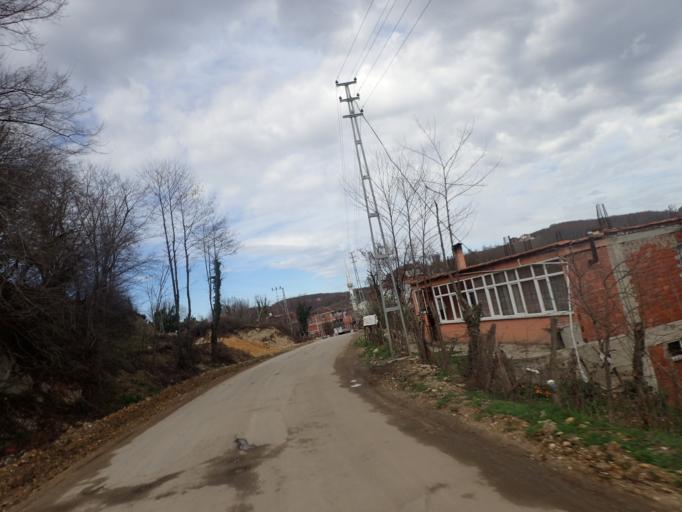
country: TR
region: Ordu
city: Kumru
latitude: 40.9407
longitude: 37.2606
